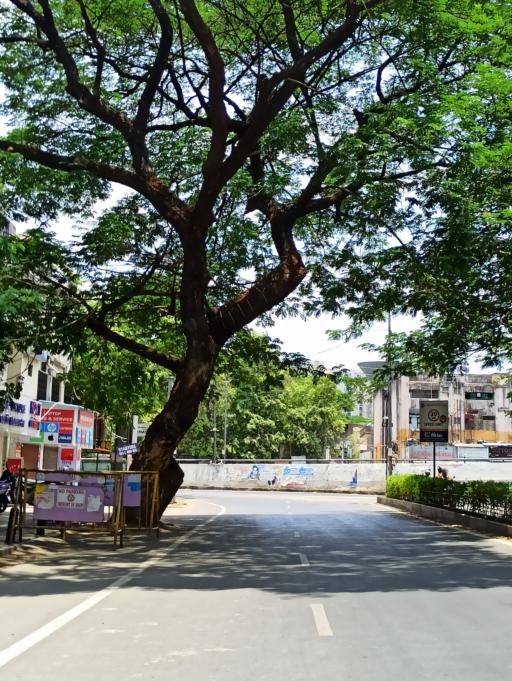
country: IN
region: Tamil Nadu
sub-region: Thiruvallur
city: Ambattur
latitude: 13.0829
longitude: 80.1992
